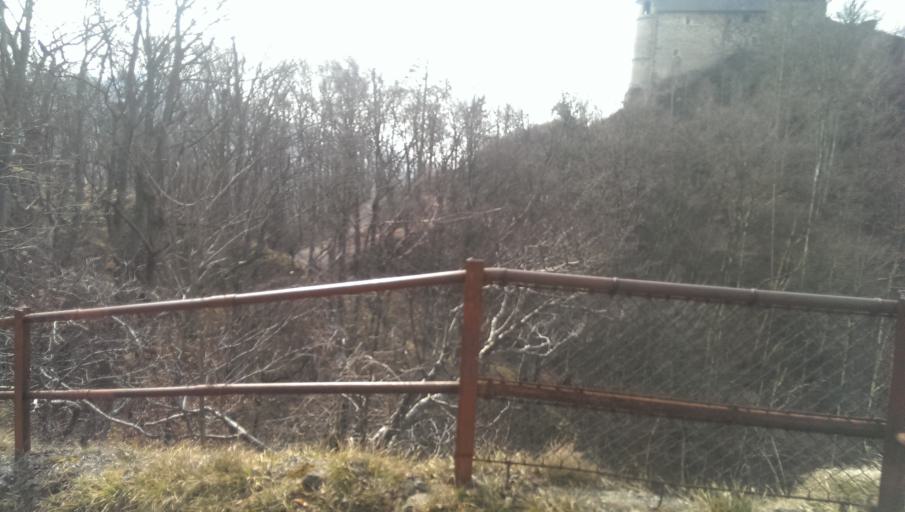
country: AT
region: Styria
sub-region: Graz Stadt
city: Goesting
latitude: 47.1047
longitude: 15.3828
